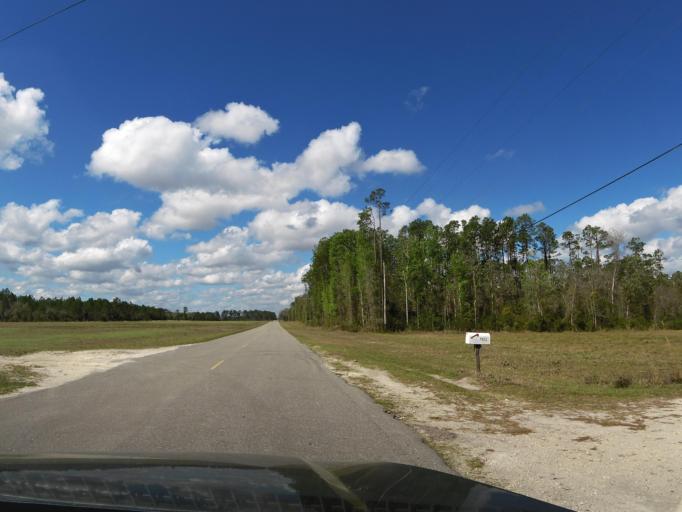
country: US
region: Florida
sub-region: Clay County
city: Green Cove Springs
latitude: 29.8680
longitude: -81.6839
